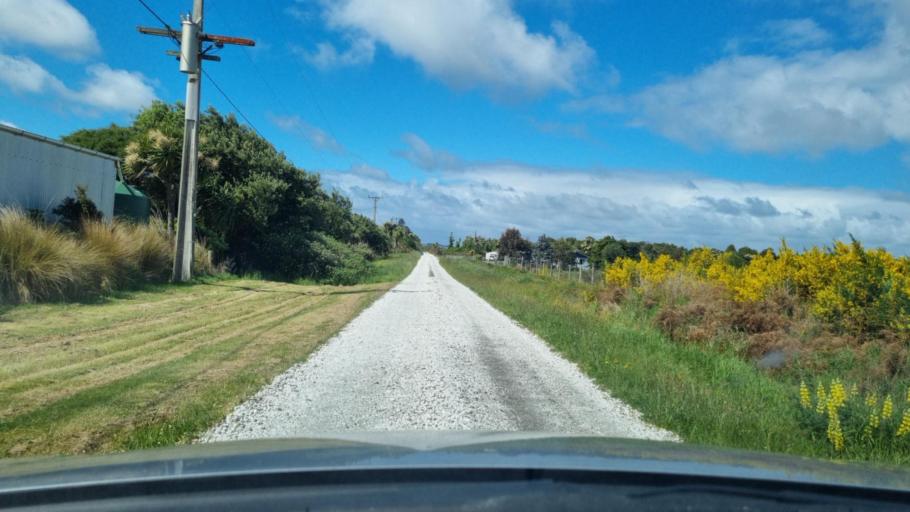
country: NZ
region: Southland
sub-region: Invercargill City
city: Invercargill
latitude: -46.4507
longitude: 168.3167
